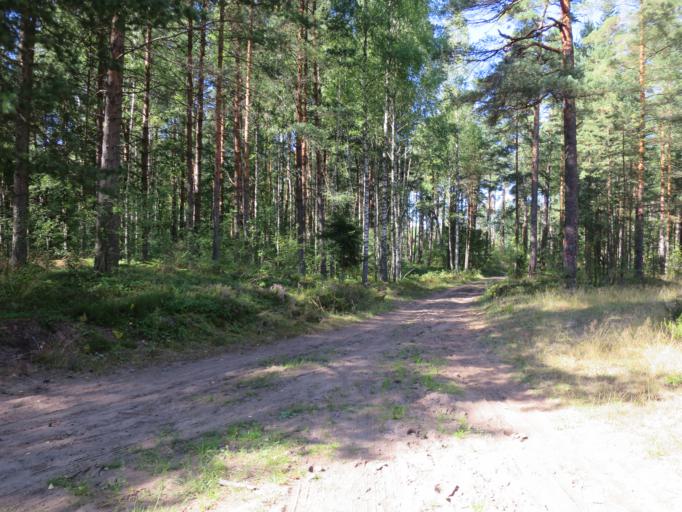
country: LV
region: Riga
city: Jaunciems
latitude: 57.0670
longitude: 24.2236
